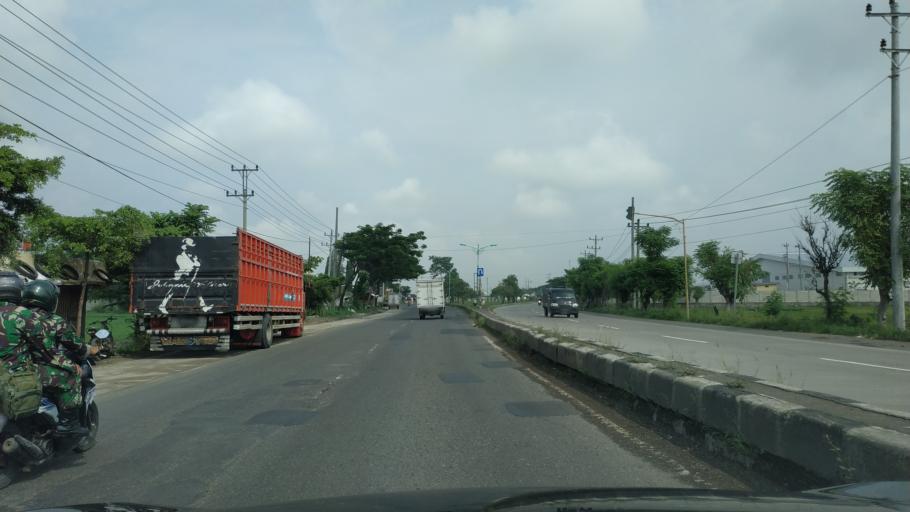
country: ID
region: Central Java
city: Bulakamba
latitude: -6.8724
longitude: 108.9080
